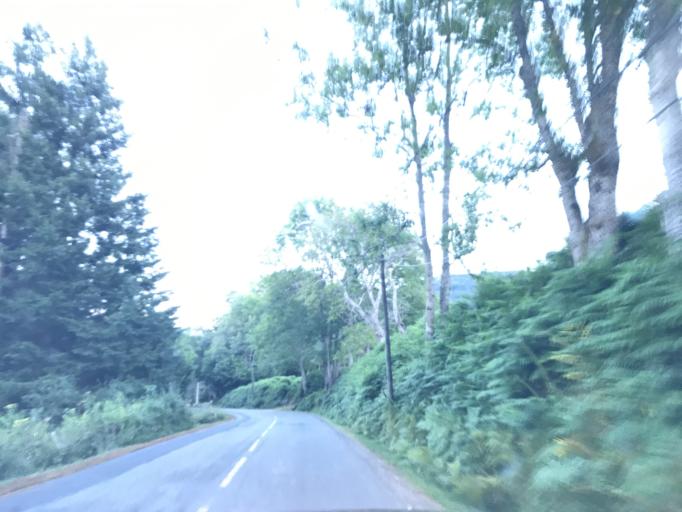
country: FR
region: Auvergne
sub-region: Departement du Puy-de-Dome
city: Chabreloche
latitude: 45.8246
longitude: 3.7001
